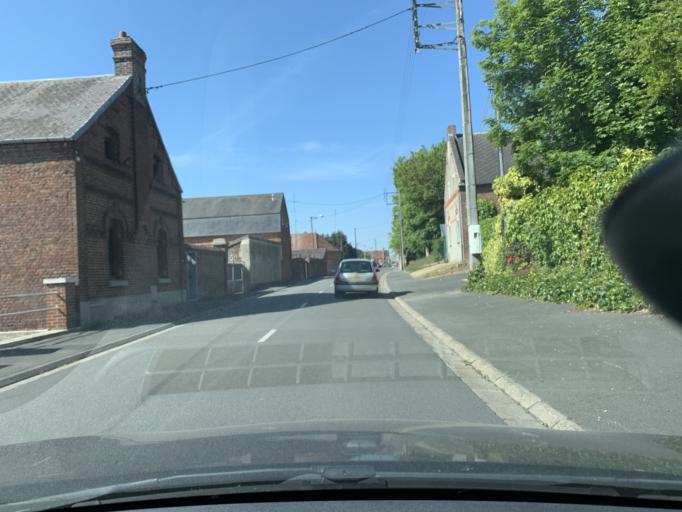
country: FR
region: Nord-Pas-de-Calais
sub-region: Departement du Nord
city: Masnieres
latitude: 50.0951
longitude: 3.2379
